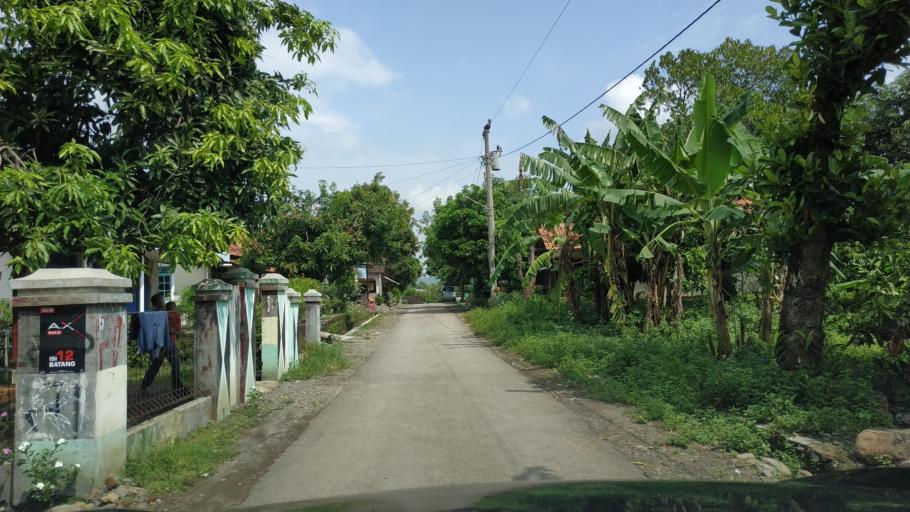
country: ID
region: Central Java
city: Margasari
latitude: -7.0912
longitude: 108.9790
